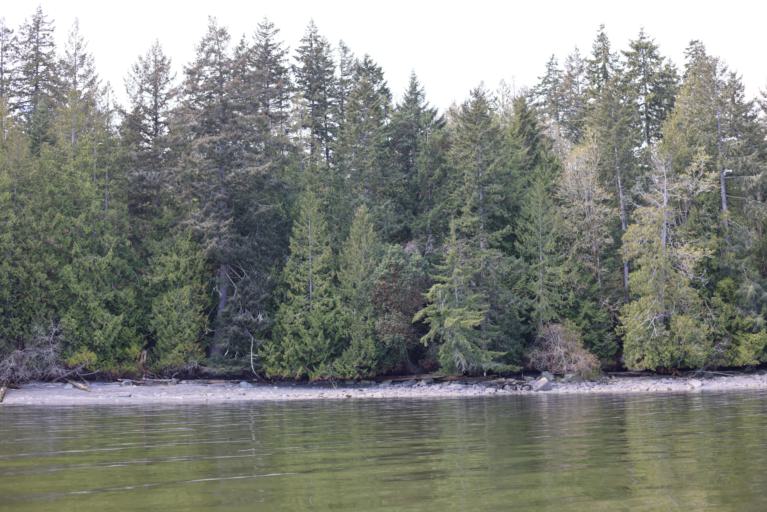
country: CA
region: British Columbia
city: North Saanich
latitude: 48.6297
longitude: -123.5282
